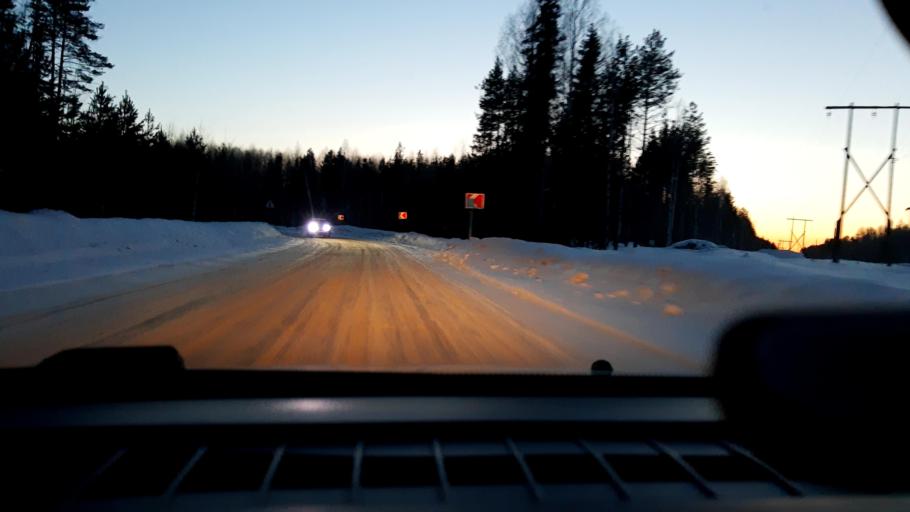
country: RU
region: Nizjnij Novgorod
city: Spasskoye
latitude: 56.1911
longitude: 45.4638
